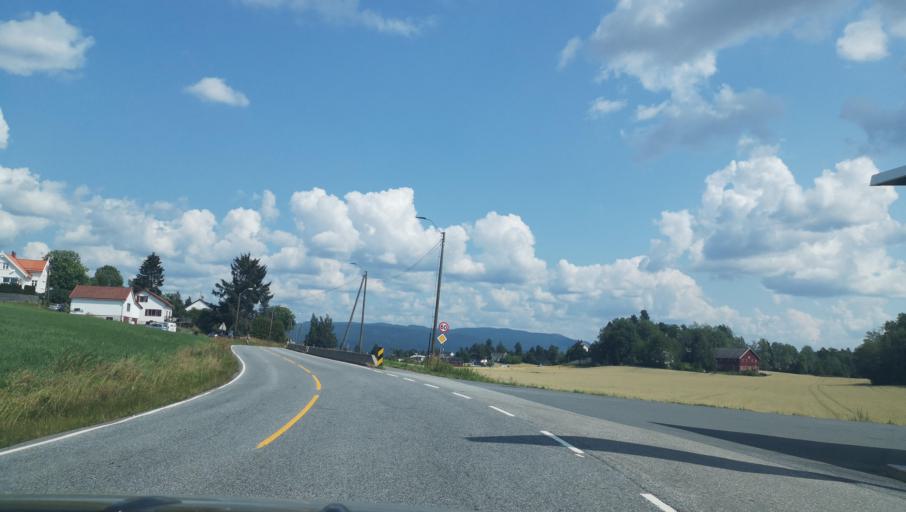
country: NO
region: Buskerud
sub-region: Ovre Eiker
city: Hokksund
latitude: 59.7296
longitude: 9.8428
